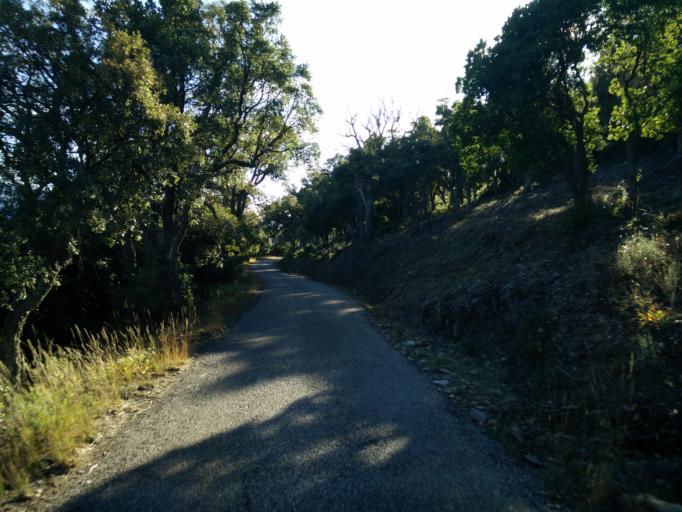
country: FR
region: Provence-Alpes-Cote d'Azur
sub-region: Departement du Var
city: Collobrieres
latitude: 43.2634
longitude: 6.2899
